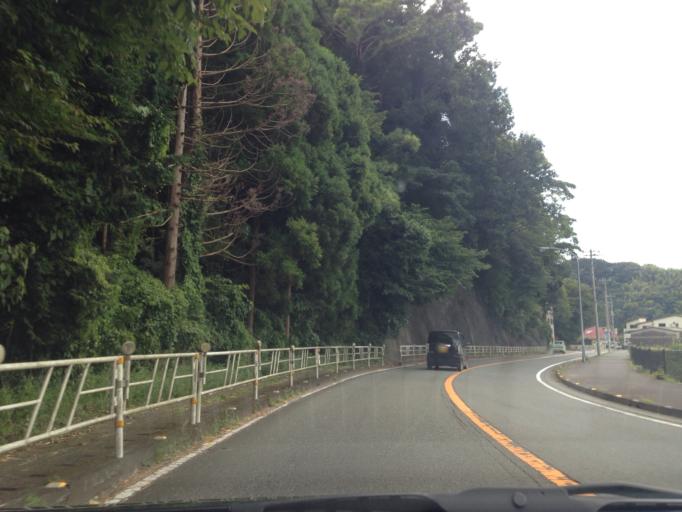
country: JP
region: Shizuoka
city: Shimoda
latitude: 34.6533
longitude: 138.8858
